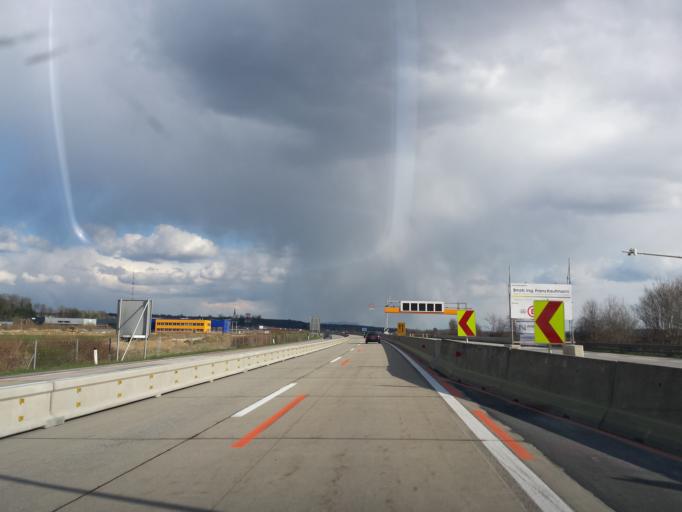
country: AT
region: Styria
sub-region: Politischer Bezirk Deutschlandsberg
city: Lannach
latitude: 46.9566
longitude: 15.3546
